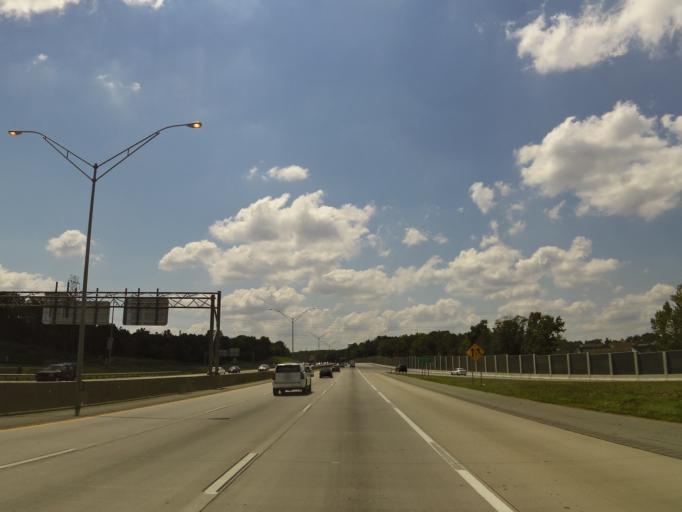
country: US
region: North Carolina
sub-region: Cabarrus County
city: Harrisburg
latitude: 35.3455
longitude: -80.7363
